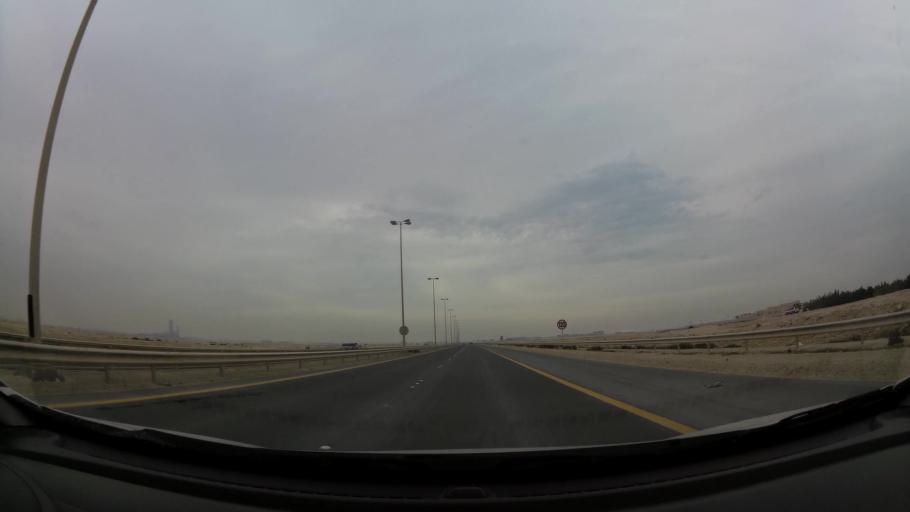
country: BH
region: Central Governorate
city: Dar Kulayb
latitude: 26.0160
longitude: 50.6070
